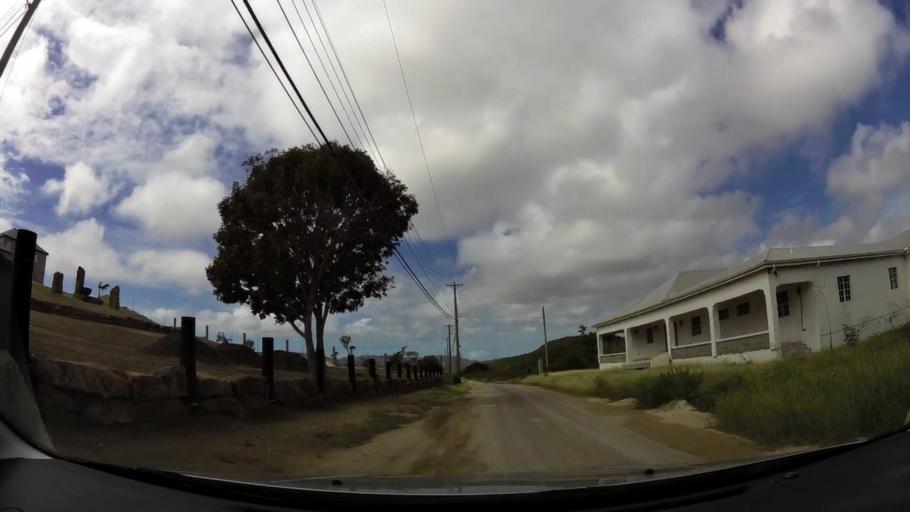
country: AG
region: Saint Paul
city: Liberta
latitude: 17.0552
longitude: -61.7329
